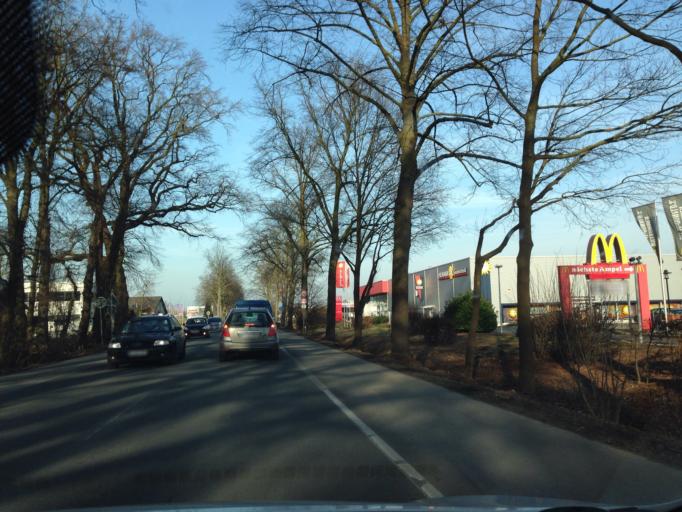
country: DE
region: North Rhine-Westphalia
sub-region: Regierungsbezirk Munster
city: Muenster
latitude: 51.9877
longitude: 7.6629
